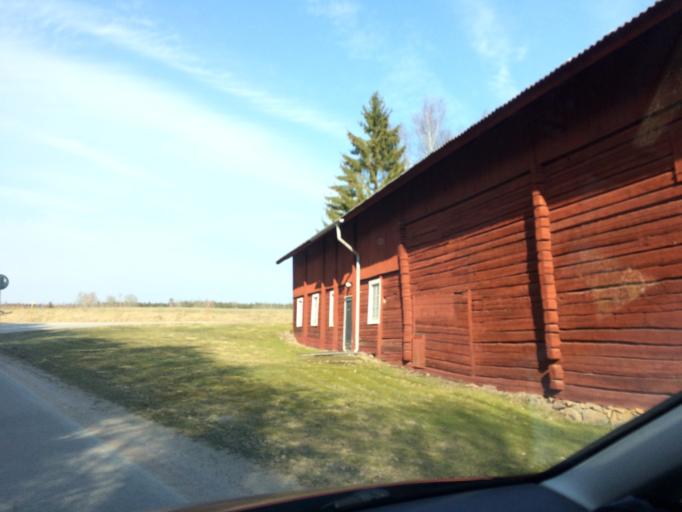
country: SE
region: Soedermanland
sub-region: Katrineholms Kommun
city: Katrineholm
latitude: 59.0904
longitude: 16.2168
